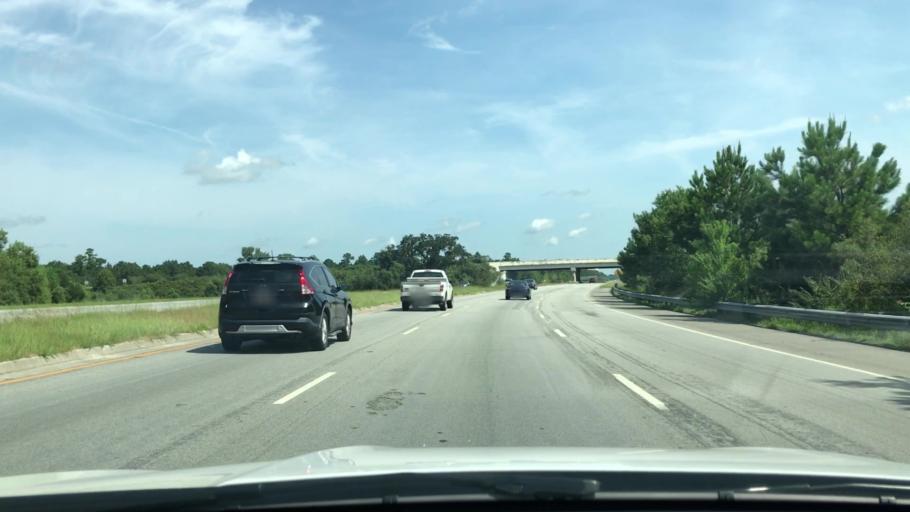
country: US
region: South Carolina
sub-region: Berkeley County
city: Goose Creek
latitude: 32.9716
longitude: -80.0457
